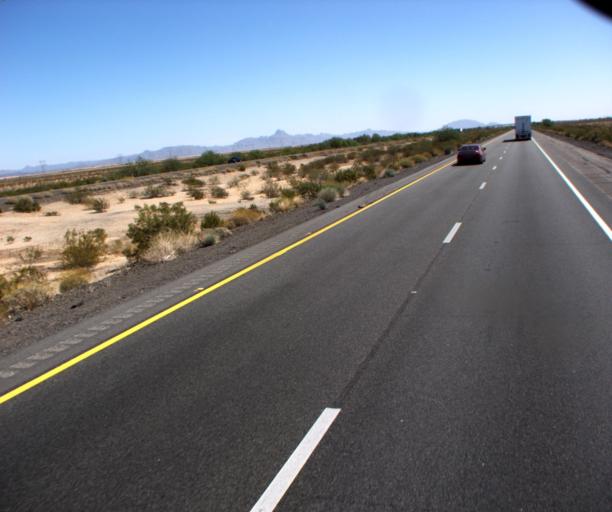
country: US
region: Arizona
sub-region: La Paz County
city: Salome
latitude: 33.5718
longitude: -113.3735
